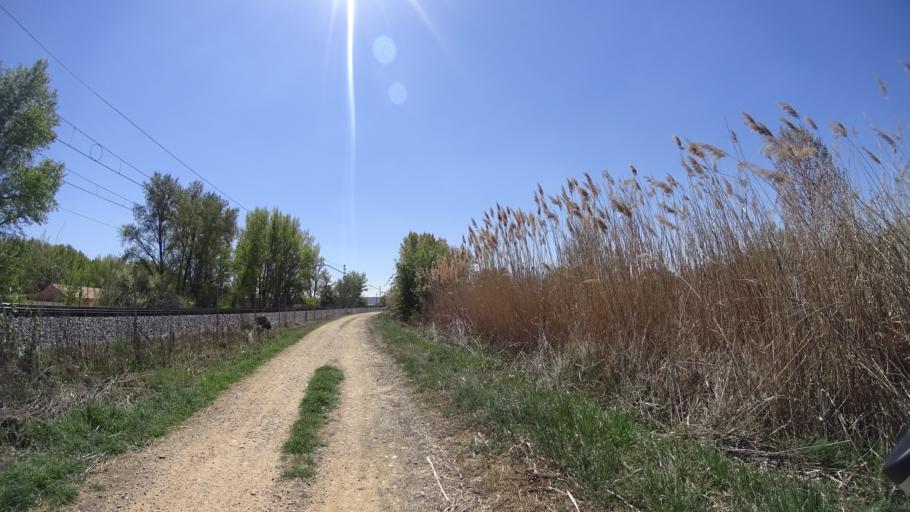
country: ES
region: Castille and Leon
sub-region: Provincia de Valladolid
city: Cubillas de Santa Marta
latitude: 41.8042
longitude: -4.5827
